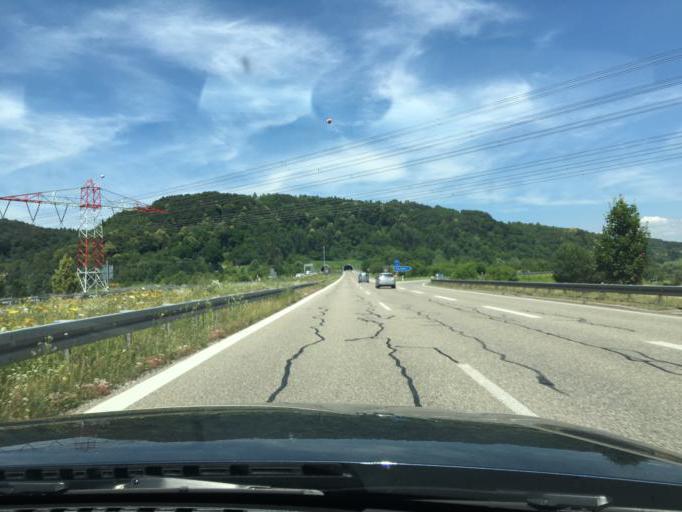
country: DE
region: Baden-Wuerttemberg
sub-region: Freiburg Region
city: Rheinfelden (Baden)
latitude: 47.5655
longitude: 7.7597
